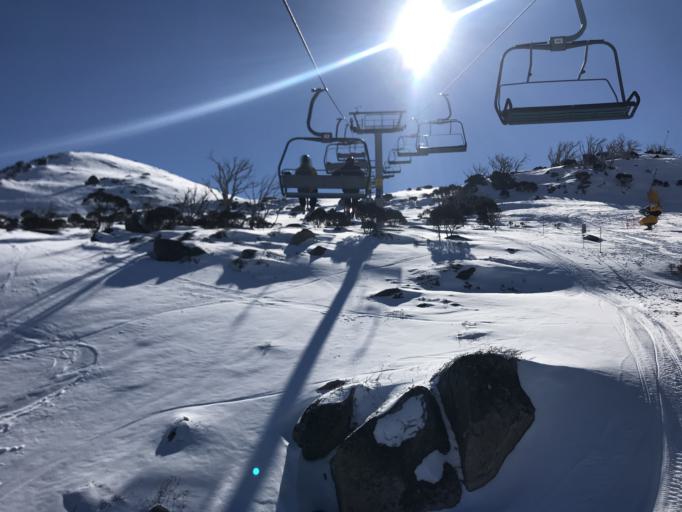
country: AU
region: New South Wales
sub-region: Snowy River
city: Jindabyne
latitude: -36.3807
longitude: 148.3969
